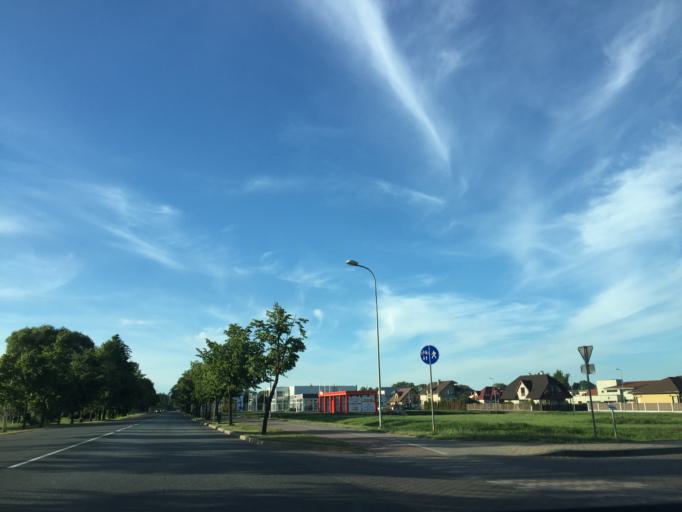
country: LV
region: Ventspils
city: Ventspils
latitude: 57.3760
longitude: 21.5658
